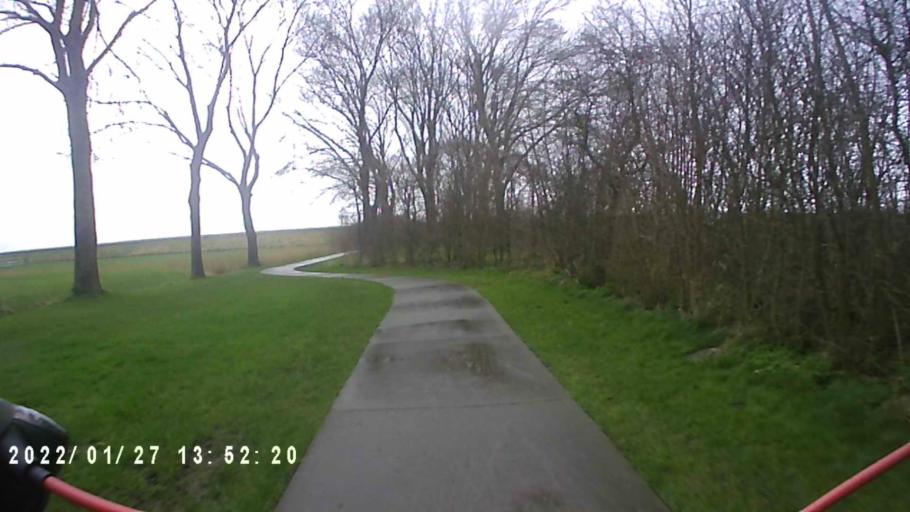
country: NL
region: Friesland
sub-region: Gemeente Kollumerland en Nieuwkruisland
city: Kollum
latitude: 53.3069
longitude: 6.1893
